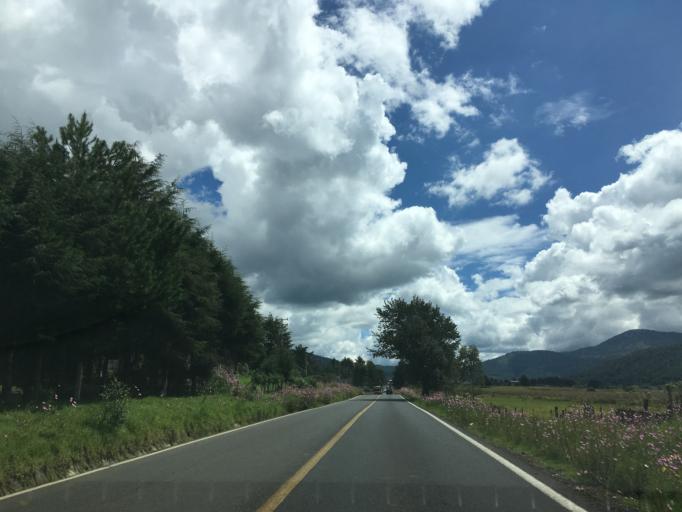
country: MX
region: Michoacan
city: Nahuatzen
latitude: 19.6610
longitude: -101.9333
